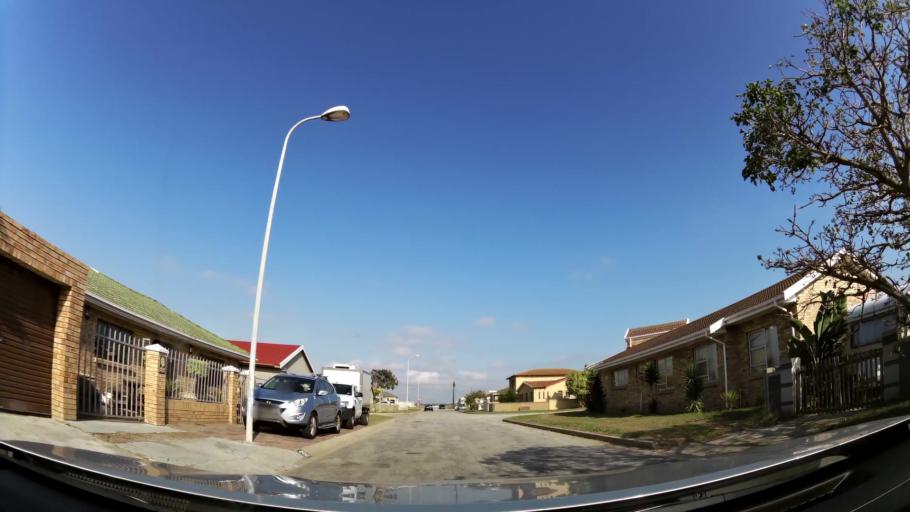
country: ZA
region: Eastern Cape
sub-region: Nelson Mandela Bay Metropolitan Municipality
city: Port Elizabeth
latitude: -33.9220
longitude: 25.5255
